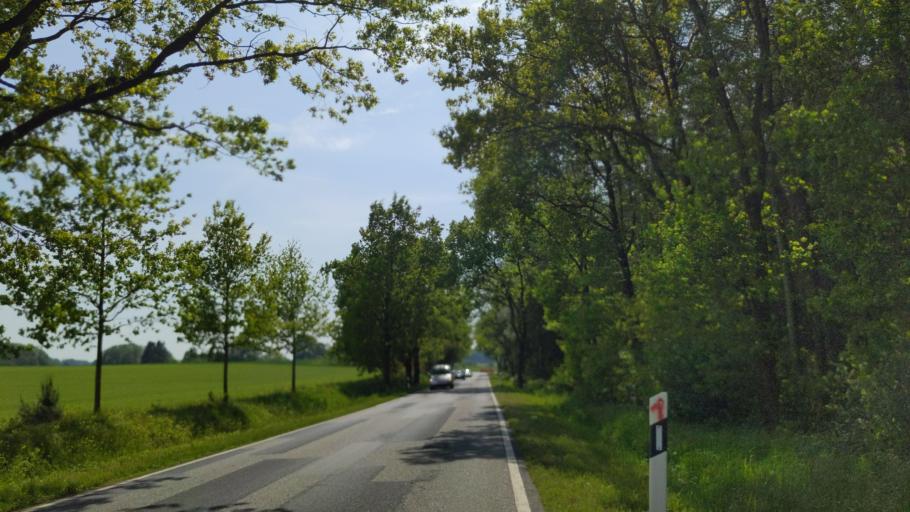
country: DE
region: Mecklenburg-Vorpommern
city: Selmsdorf
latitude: 53.8723
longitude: 10.8343
